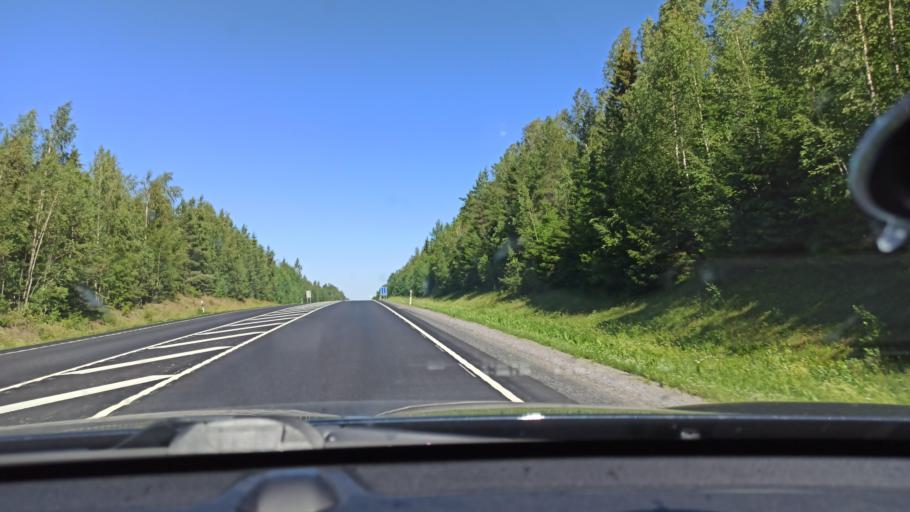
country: FI
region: Ostrobothnia
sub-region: Vaasa
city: Oravais
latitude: 63.2701
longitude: 22.3093
